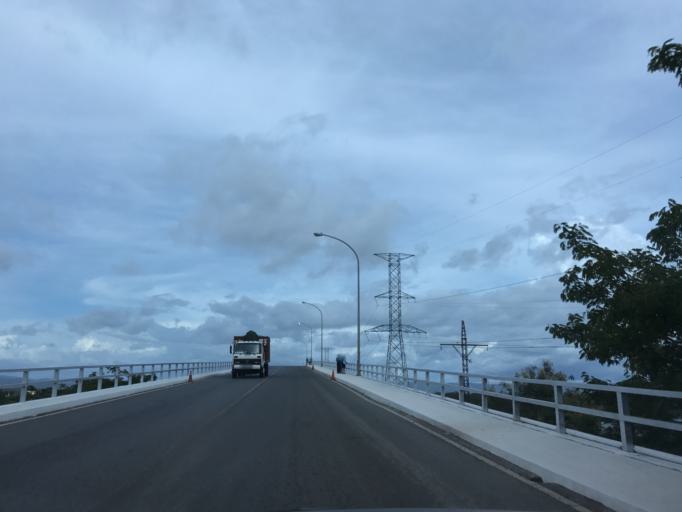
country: GT
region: Izabal
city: Morales
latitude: 15.6578
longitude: -89.0004
